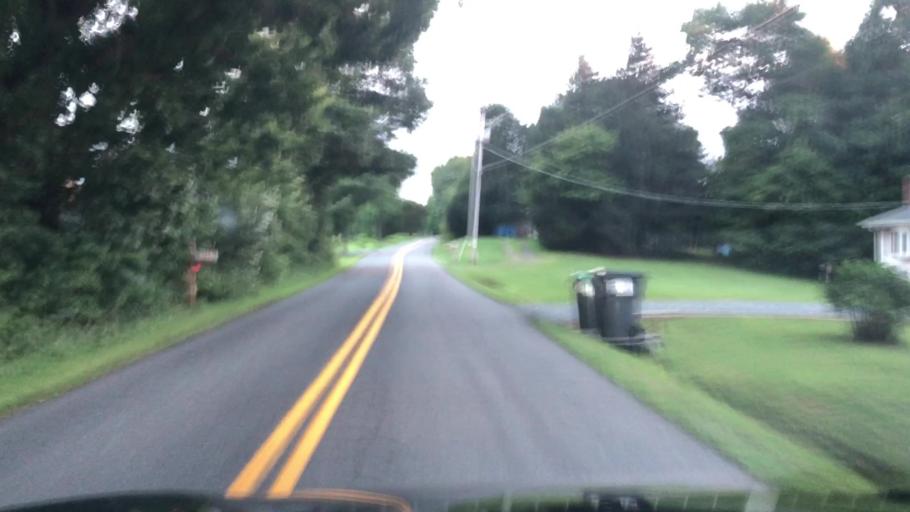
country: US
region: Virginia
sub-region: Stafford County
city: Stafford
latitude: 38.4871
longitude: -77.5795
